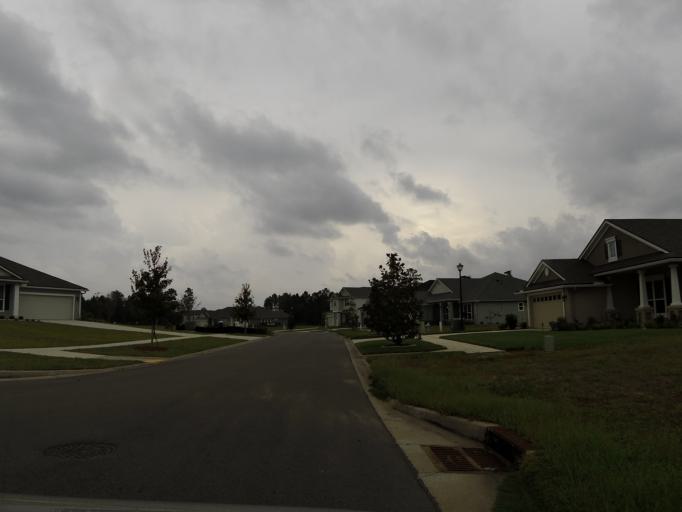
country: US
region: Florida
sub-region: Clay County
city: Middleburg
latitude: 30.1093
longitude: -81.8633
